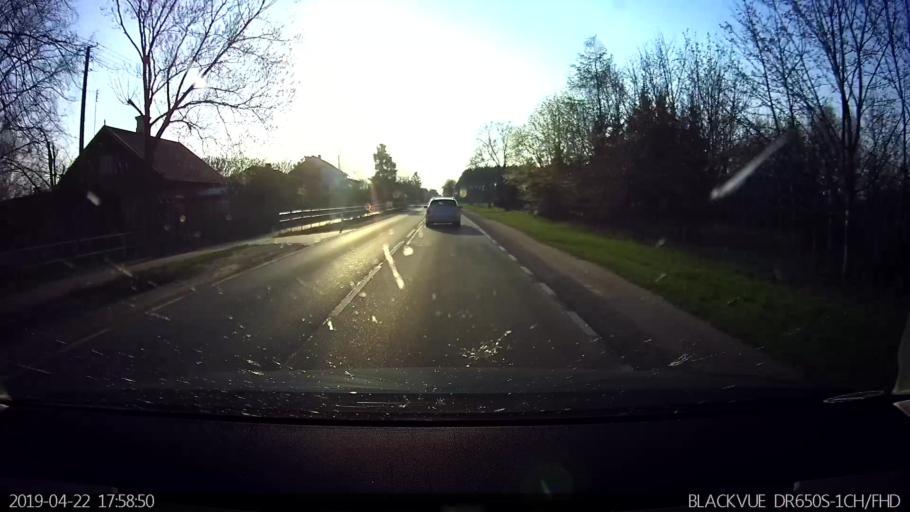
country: PL
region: Masovian Voivodeship
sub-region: Powiat wegrowski
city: Korytnica
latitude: 52.4727
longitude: 21.8712
